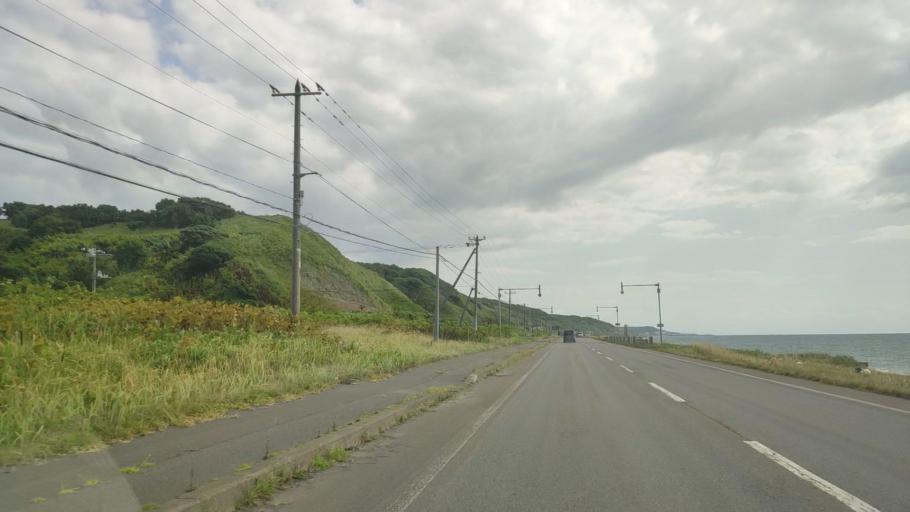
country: JP
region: Hokkaido
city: Rumoi
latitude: 44.1953
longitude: 141.6580
